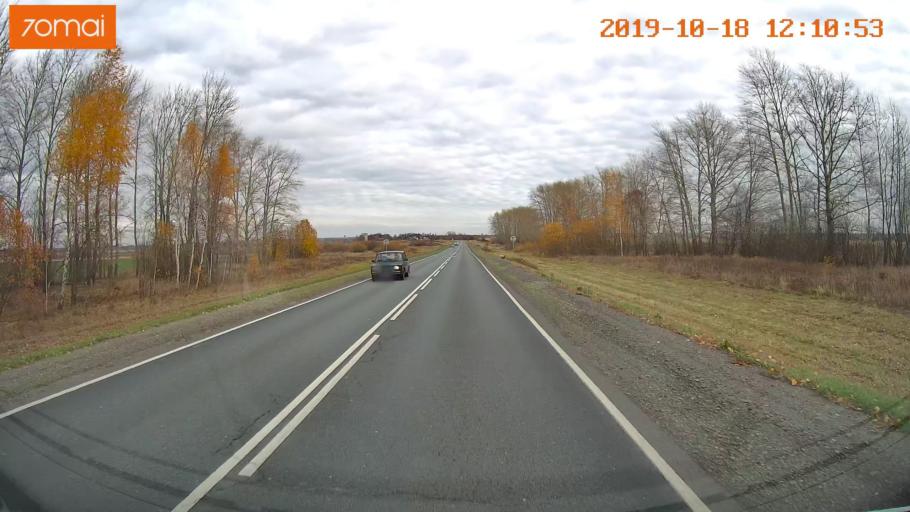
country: RU
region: Rjazan
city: Zakharovo
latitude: 54.3962
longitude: 39.3405
